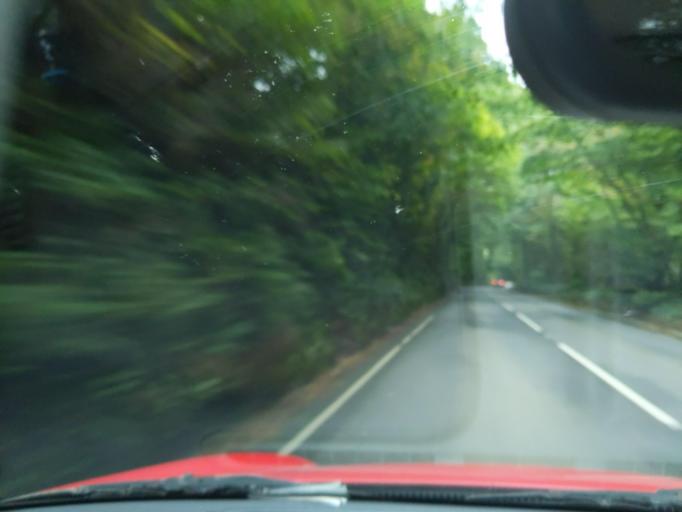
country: GB
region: England
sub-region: Devon
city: Great Torrington
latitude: 50.9411
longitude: -4.1419
